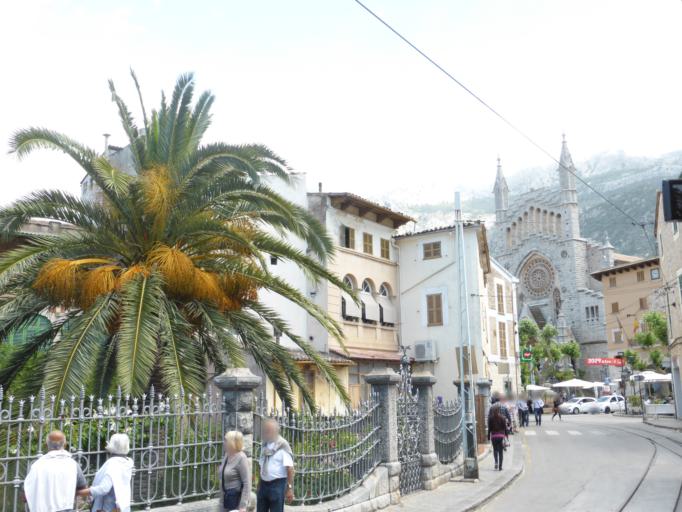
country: ES
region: Balearic Islands
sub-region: Illes Balears
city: Soller
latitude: 39.7672
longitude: 2.7142
